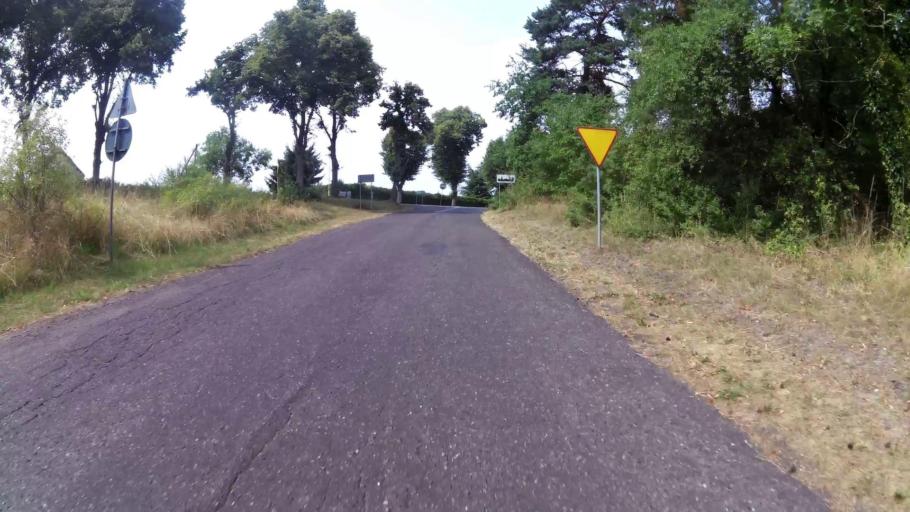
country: PL
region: West Pomeranian Voivodeship
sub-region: Powiat gryfinski
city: Moryn
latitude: 52.8479
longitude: 14.3977
